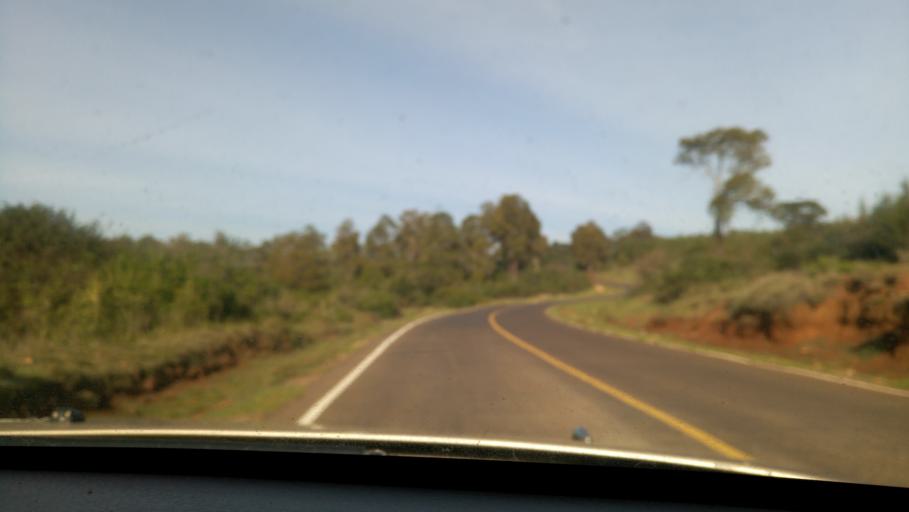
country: KE
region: Laikipia
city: Nyahururu
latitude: -0.0124
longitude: 36.3433
